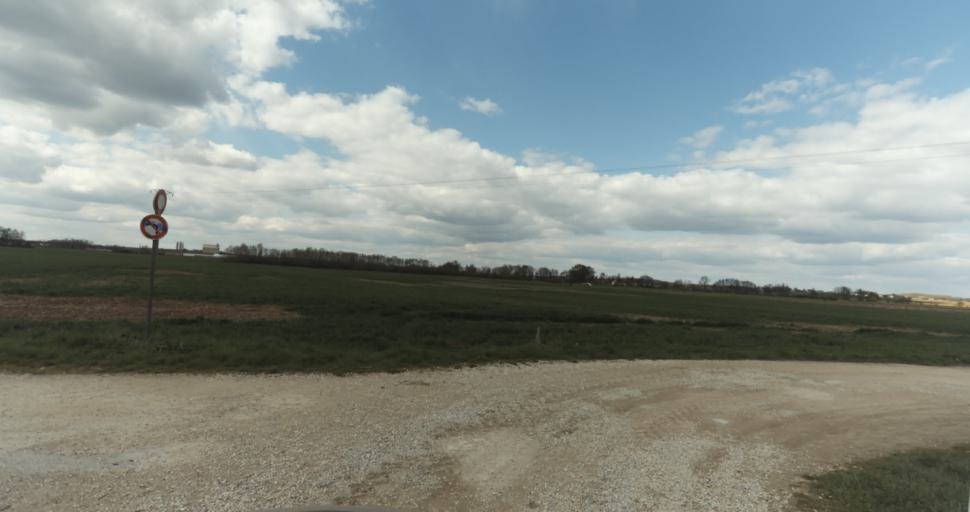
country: FR
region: Bourgogne
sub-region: Departement de la Cote-d'Or
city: Auxonne
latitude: 47.1980
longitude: 5.4120
